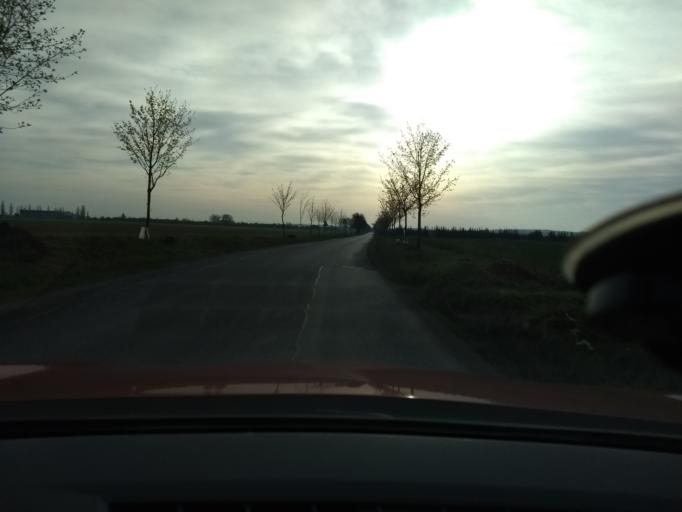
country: CZ
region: Central Bohemia
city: Jenec
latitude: 50.0686
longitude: 14.2111
